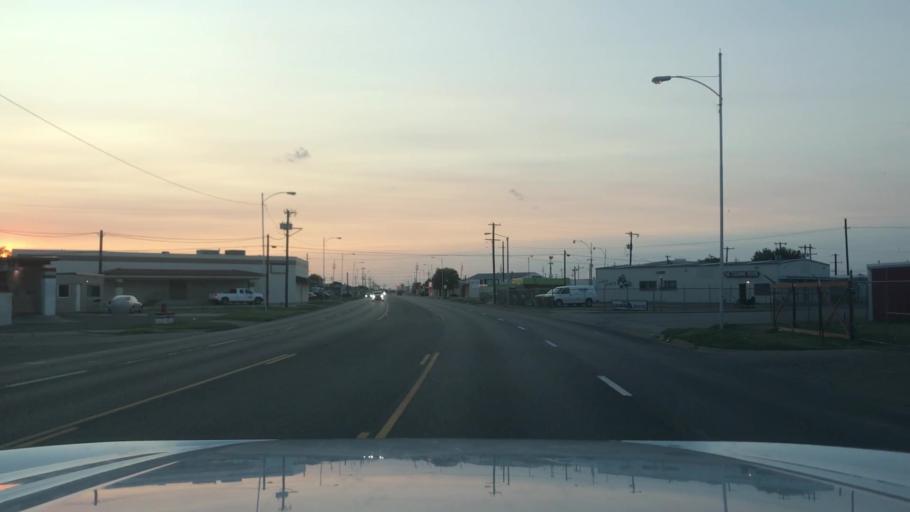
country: US
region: Texas
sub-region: Lubbock County
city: Lubbock
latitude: 33.5963
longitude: -101.8572
